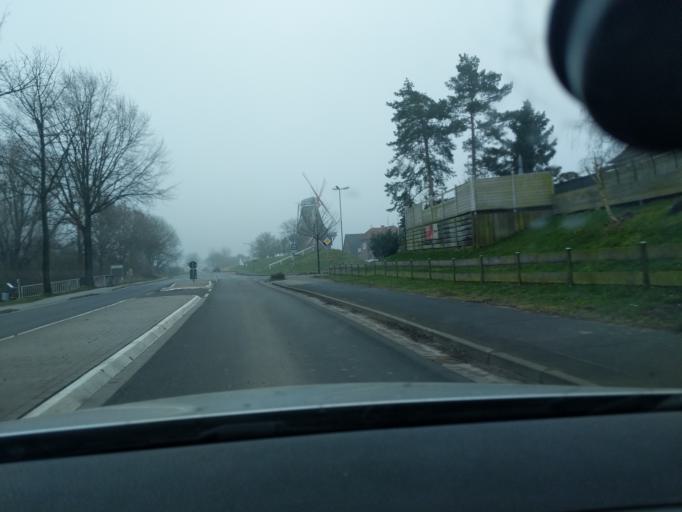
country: DE
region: Lower Saxony
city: Jork
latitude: 53.5404
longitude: 9.6904
